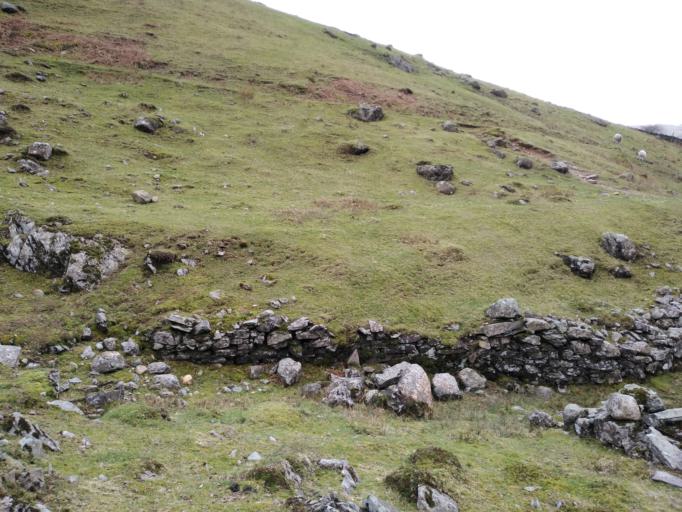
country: GB
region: England
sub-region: Cumbria
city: Ambleside
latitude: 54.4794
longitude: -3.0198
